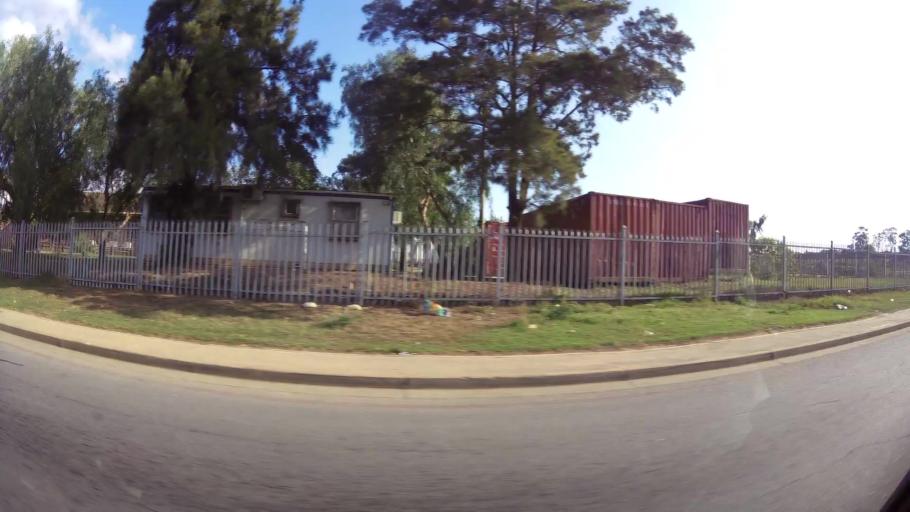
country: ZA
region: Eastern Cape
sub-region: Nelson Mandela Bay Metropolitan Municipality
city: Uitenhage
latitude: -33.7529
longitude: 25.3858
